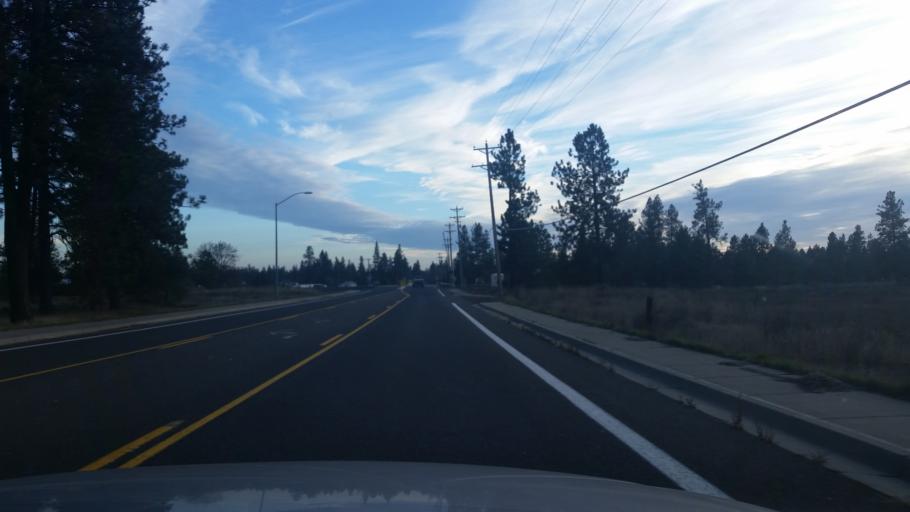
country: US
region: Washington
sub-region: Spokane County
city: Cheney
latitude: 47.4689
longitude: -117.6077
